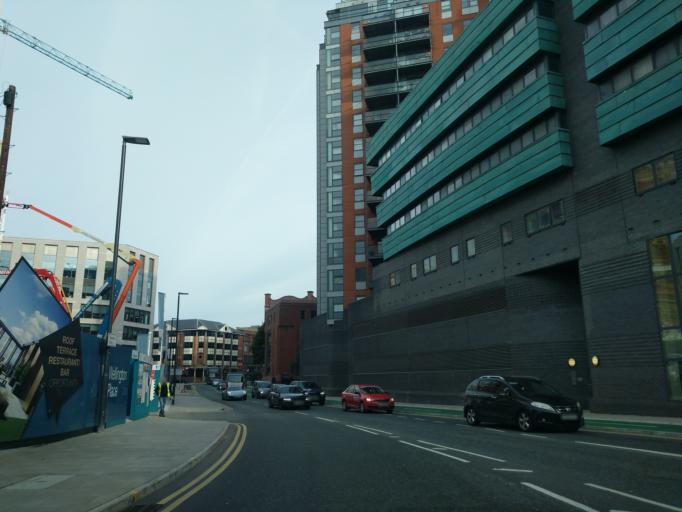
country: GB
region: England
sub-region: City and Borough of Leeds
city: Leeds
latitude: 53.7956
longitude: -1.5541
